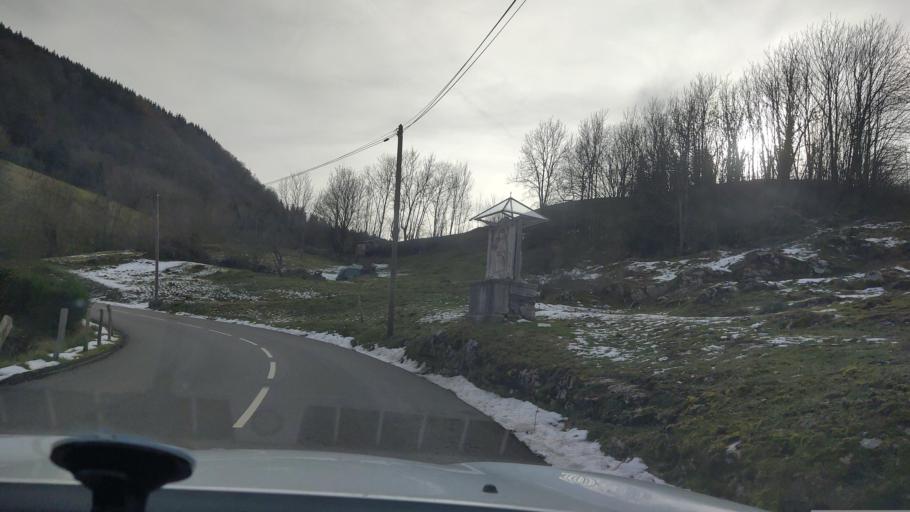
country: FR
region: Rhone-Alpes
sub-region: Departement de la Savoie
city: Coise-Saint-Jean-Pied-Gauthier
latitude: 45.5949
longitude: 6.1374
